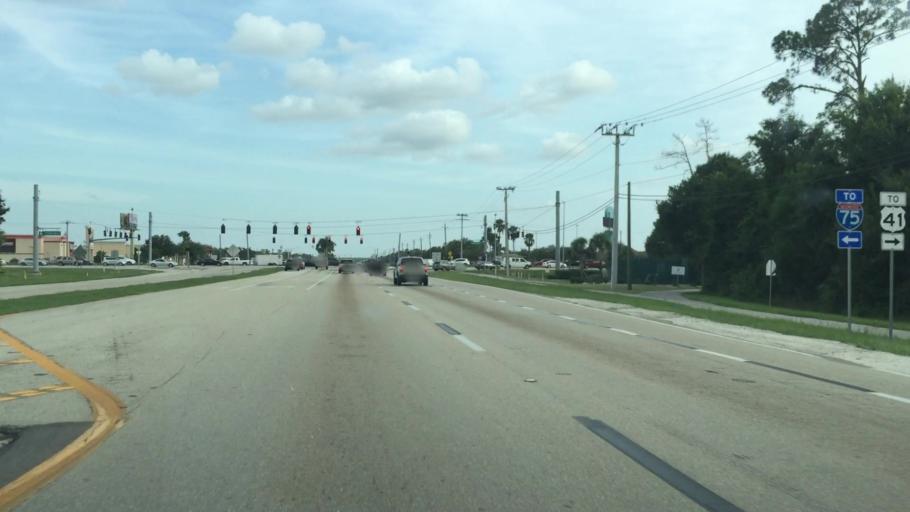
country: US
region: Florida
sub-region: Lee County
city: Fort Myers
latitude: 26.6143
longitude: -81.8114
